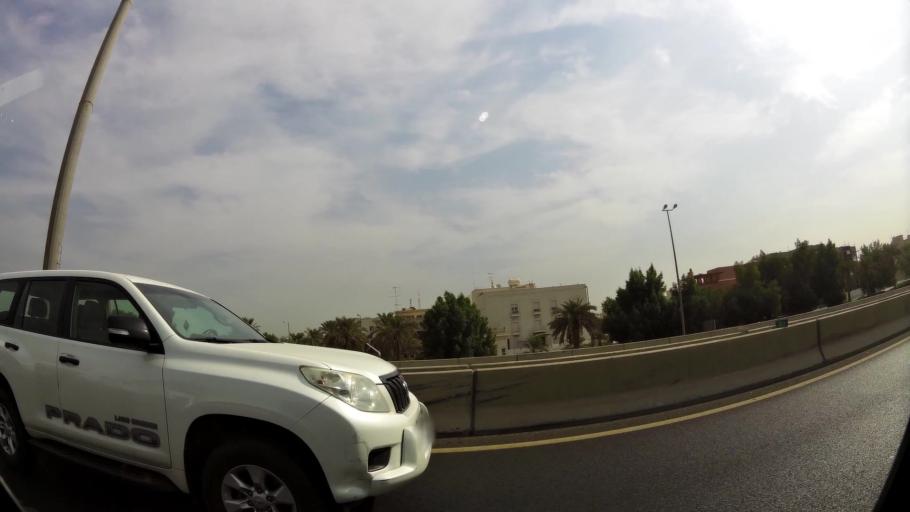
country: KW
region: Al Asimah
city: Ash Shamiyah
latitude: 29.3303
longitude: 47.9716
